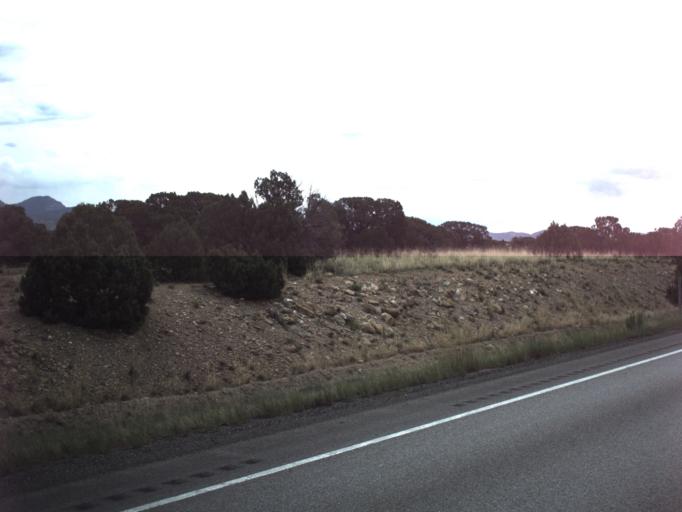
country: US
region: Utah
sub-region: Carbon County
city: East Carbon City
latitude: 39.4198
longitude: -110.4404
